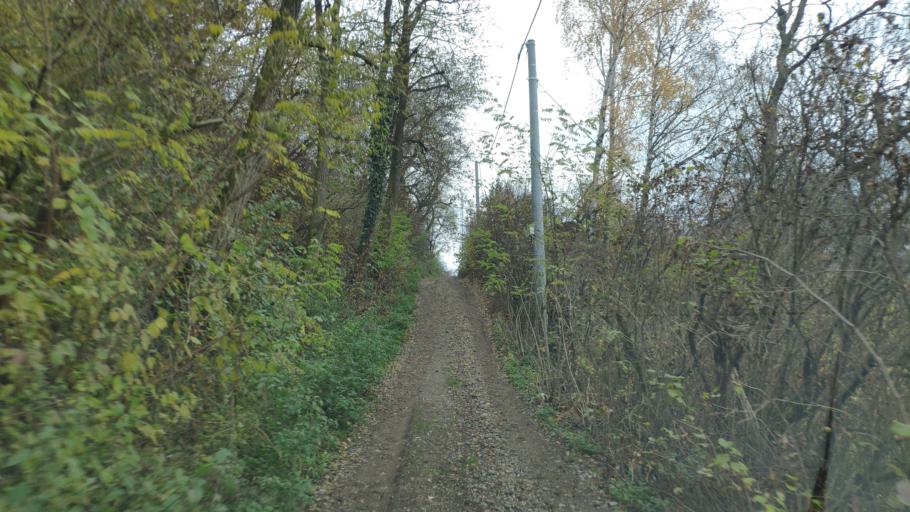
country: SK
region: Kosicky
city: Kosice
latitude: 48.6974
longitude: 21.2908
